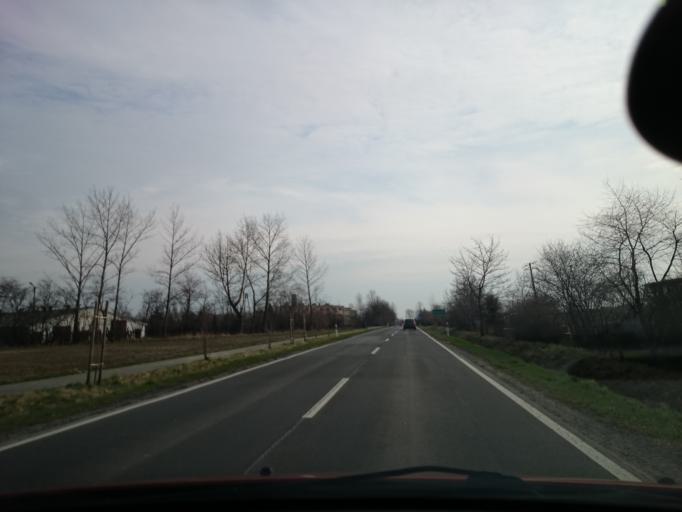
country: PL
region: Opole Voivodeship
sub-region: Powiat nyski
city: Glucholazy
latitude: 50.3190
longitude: 17.4253
